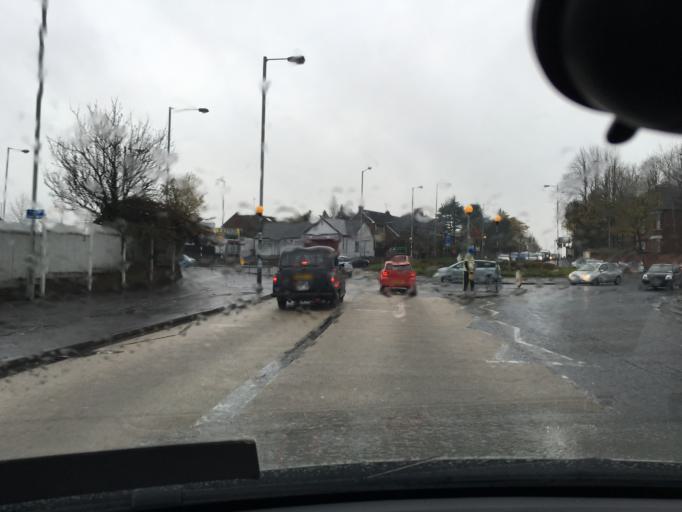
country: GB
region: Northern Ireland
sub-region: City of Belfast
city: Belfast
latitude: 54.5777
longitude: -5.9797
